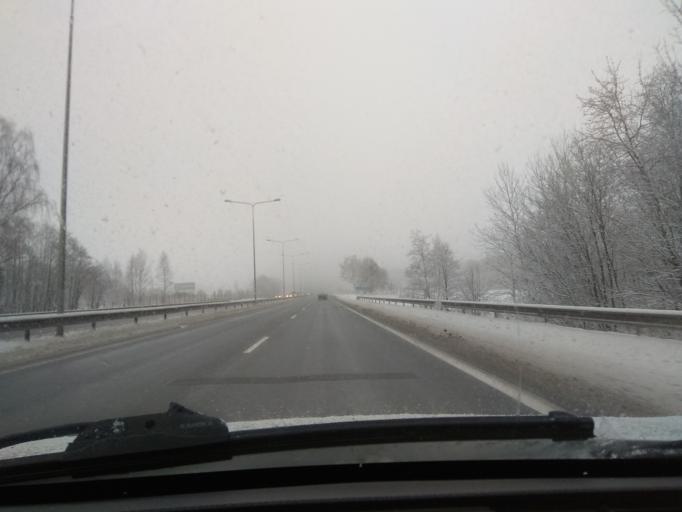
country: LT
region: Kauno apskritis
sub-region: Kauno rajonas
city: Karmelava
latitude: 54.8990
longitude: 24.1397
